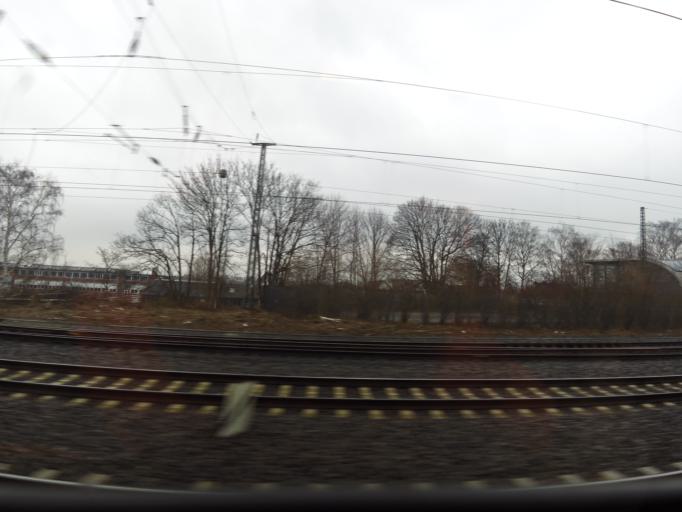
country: DE
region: North Rhine-Westphalia
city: Bad Oeynhausen
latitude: 52.2062
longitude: 8.8079
